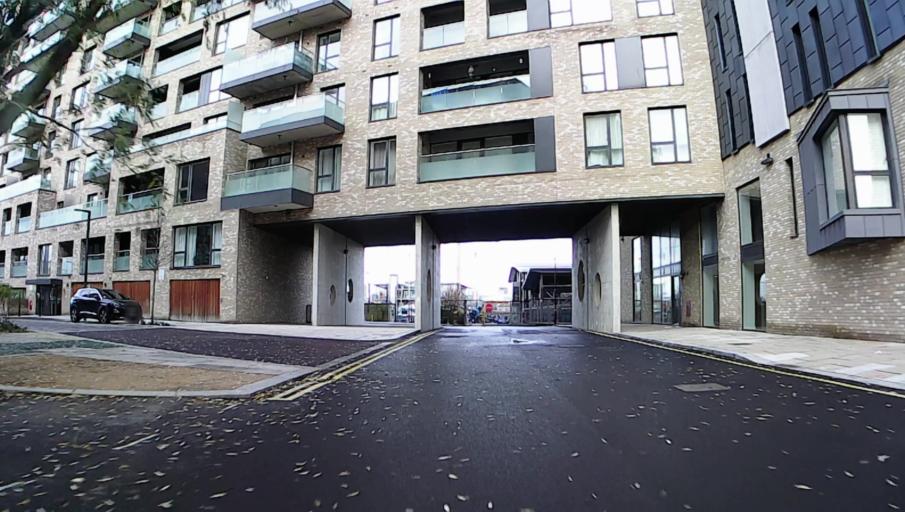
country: GB
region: England
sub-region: Greater London
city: Blackheath
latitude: 51.4938
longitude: 0.0186
